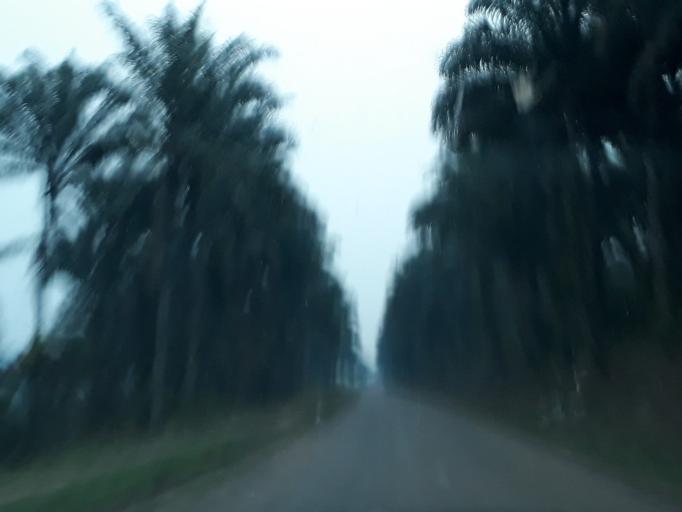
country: CD
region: Bandundu
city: Kikwit
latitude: -5.0697
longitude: 18.8696
